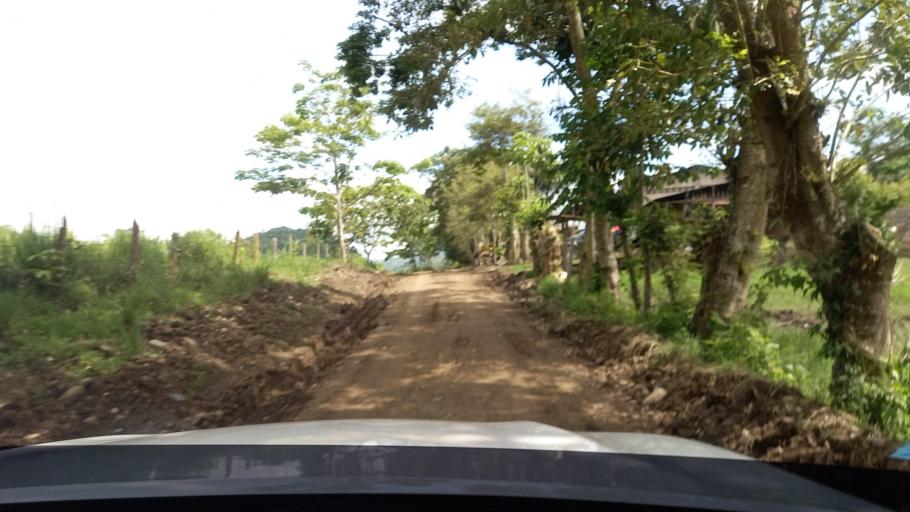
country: NI
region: Jinotega
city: San Jose de Bocay
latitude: 13.3853
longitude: -85.6890
